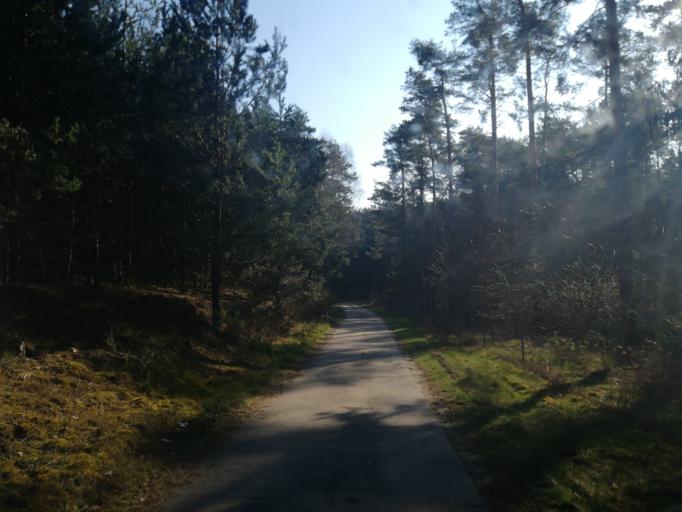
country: DE
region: Brandenburg
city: Drahnsdorf
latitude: 51.8895
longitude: 13.5496
